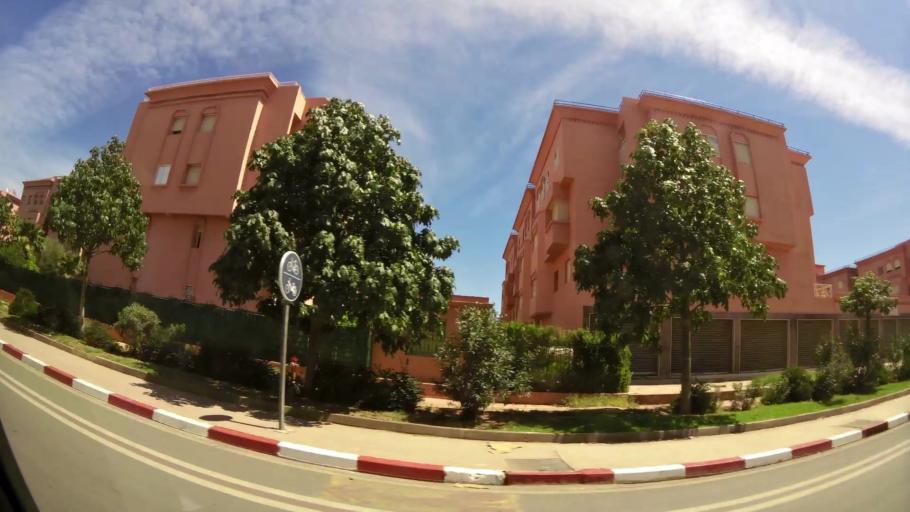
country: MA
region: Marrakech-Tensift-Al Haouz
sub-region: Marrakech
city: Marrakesh
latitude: 31.6700
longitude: -8.0085
